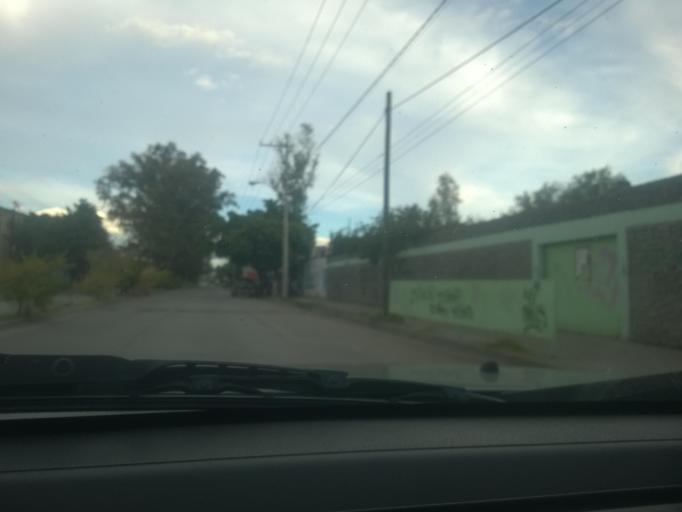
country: MX
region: Guanajuato
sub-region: Leon
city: Medina
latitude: 21.1300
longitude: -101.6391
